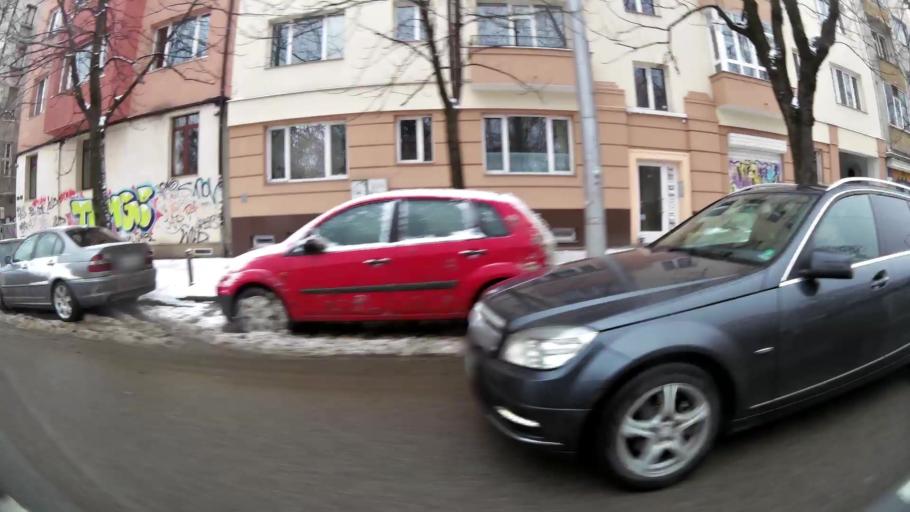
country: BG
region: Sofia-Capital
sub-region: Stolichna Obshtina
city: Sofia
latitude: 42.6959
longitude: 23.3434
